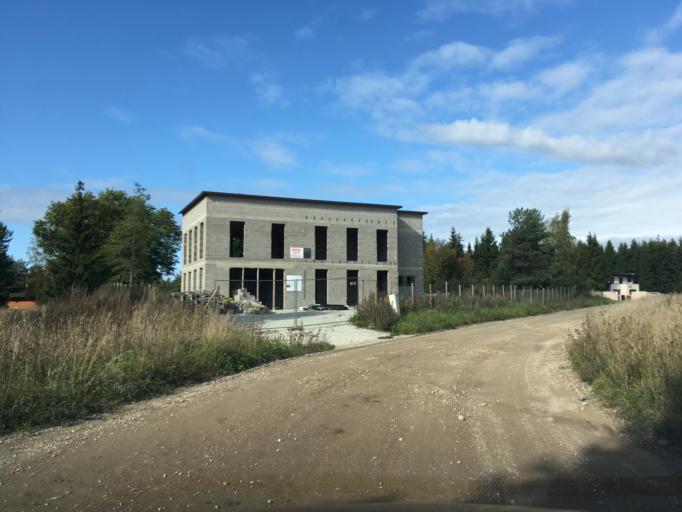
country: EE
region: Harju
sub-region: Saku vald
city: Saku
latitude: 59.3373
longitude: 24.6482
